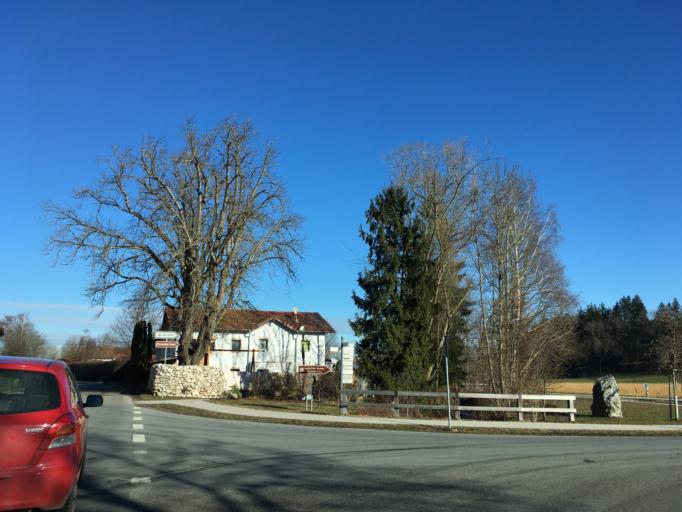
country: DE
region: Bavaria
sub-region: Upper Bavaria
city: Amerang
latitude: 47.9946
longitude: 12.3072
